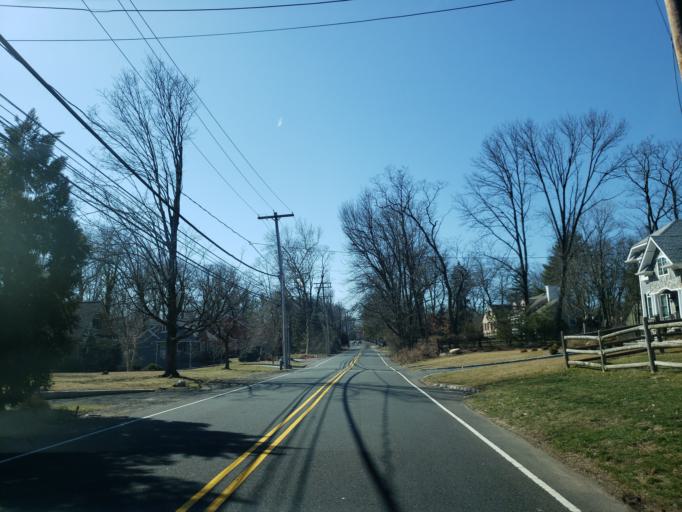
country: US
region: New Jersey
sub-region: Essex County
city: Short Hills
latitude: 40.7473
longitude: -74.3322
